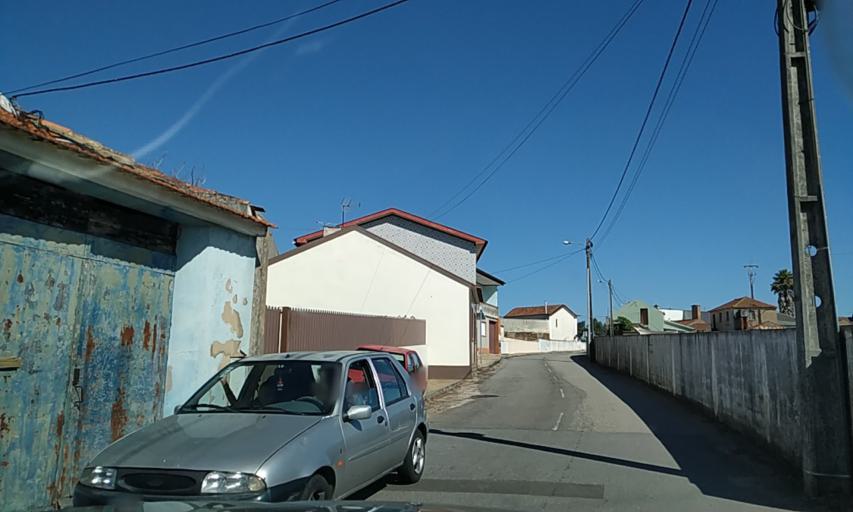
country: PT
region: Aveiro
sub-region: Estarreja
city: Salreu
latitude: 40.7492
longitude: -8.5518
